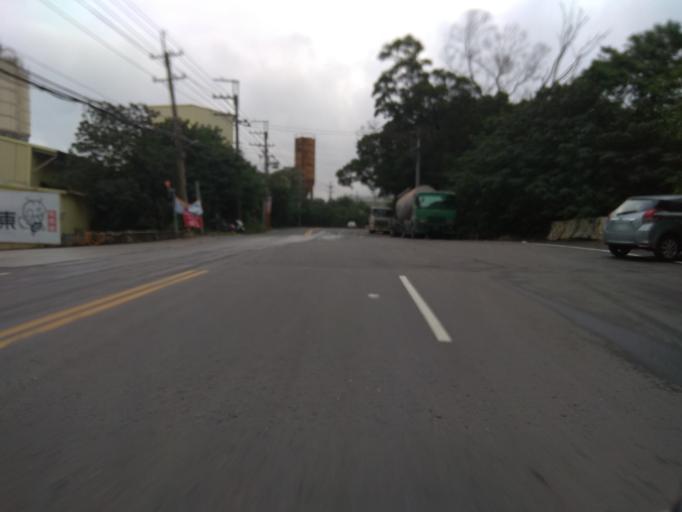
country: TW
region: Taiwan
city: Daxi
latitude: 24.9245
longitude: 121.1640
